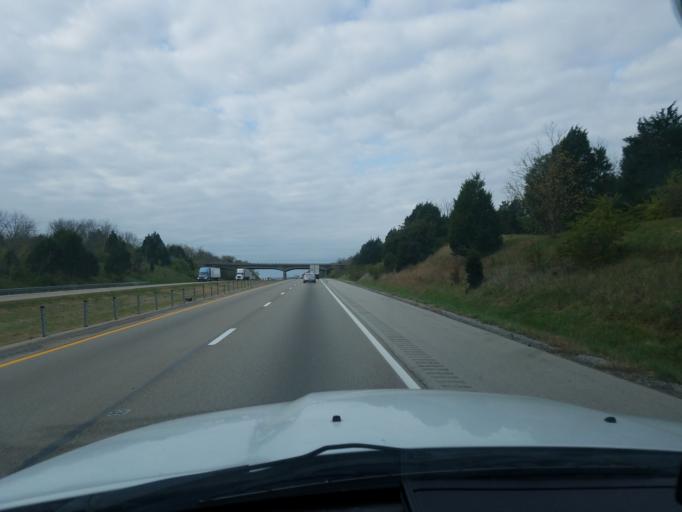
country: US
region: Kentucky
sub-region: Gallatin County
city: Warsaw
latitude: 38.7306
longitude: -84.8509
